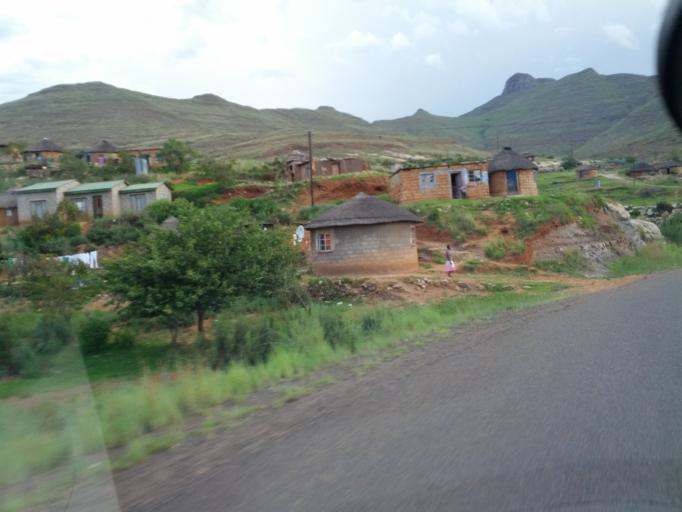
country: LS
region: Qacha's Nek
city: Qacha's Nek
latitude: -30.0772
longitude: 28.5821
